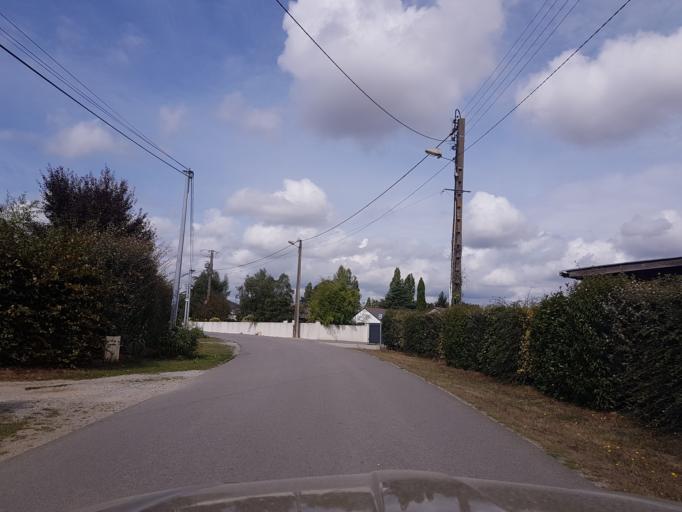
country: FR
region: Pays de la Loire
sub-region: Departement de la Loire-Atlantique
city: Petit-Mars
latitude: 47.3870
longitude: -1.4303
